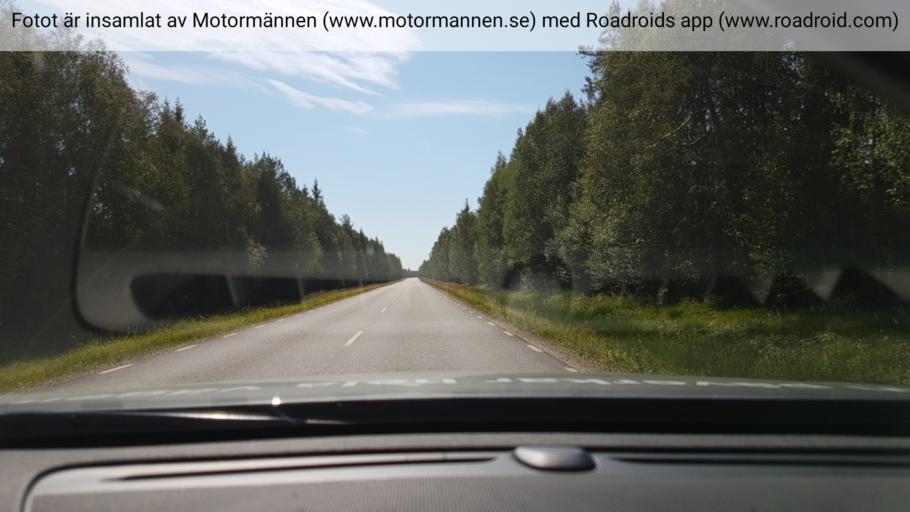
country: SE
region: Vaesterbotten
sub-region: Vindelns Kommun
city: Vindeln
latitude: 64.4062
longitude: 19.3696
